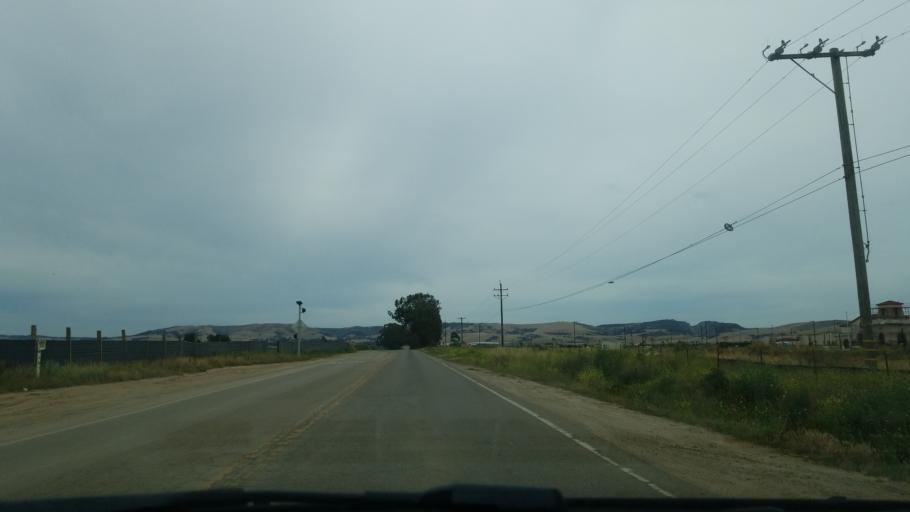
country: US
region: California
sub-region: Santa Barbara County
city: Santa Maria
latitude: 34.9201
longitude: -120.4902
